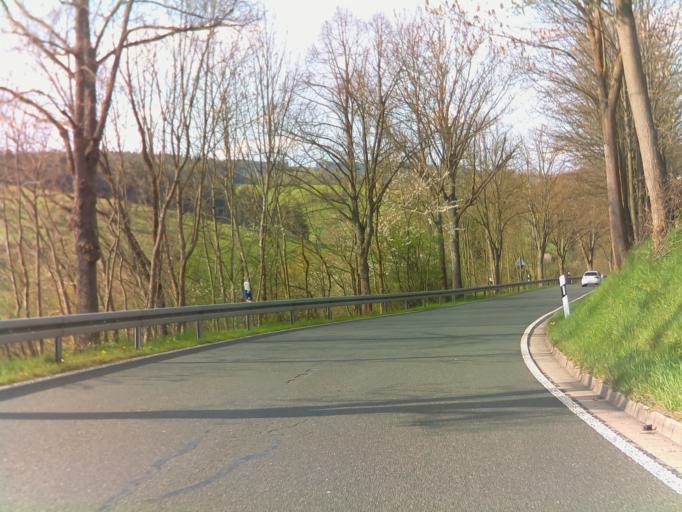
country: DE
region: Thuringia
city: Grafenthal
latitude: 50.5117
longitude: 11.2963
